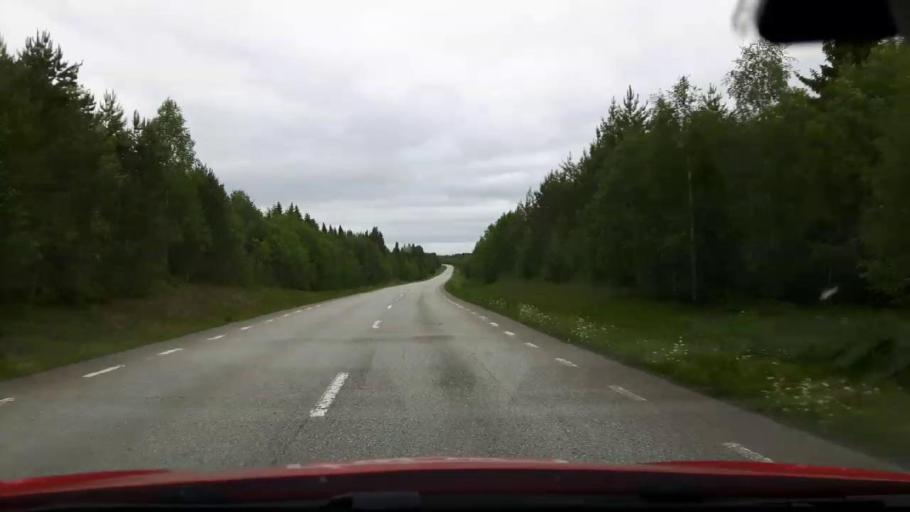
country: SE
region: Jaemtland
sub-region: OEstersunds Kommun
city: Lit
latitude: 63.5939
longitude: 14.6459
